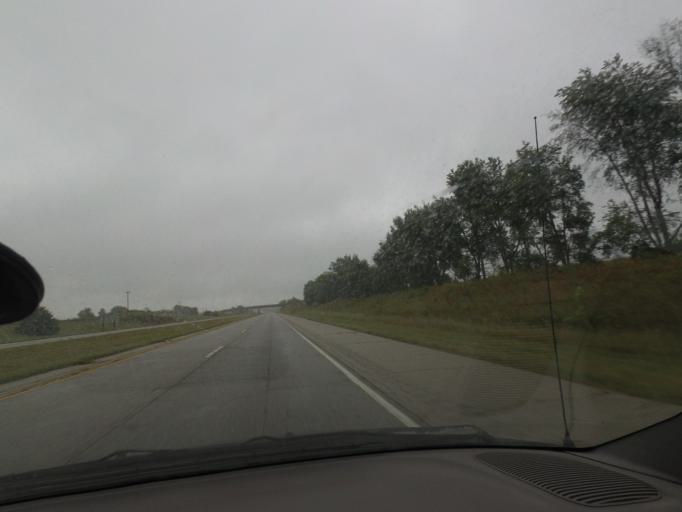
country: US
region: Illinois
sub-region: Pike County
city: Barry
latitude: 39.6962
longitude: -91.0098
